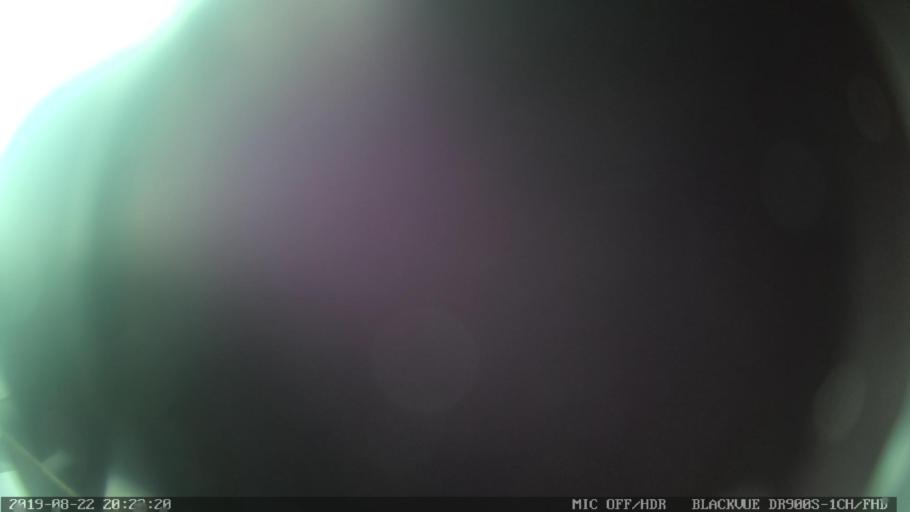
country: PT
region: Castelo Branco
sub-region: Castelo Branco
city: Castelo Branco
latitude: 39.8493
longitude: -7.5046
